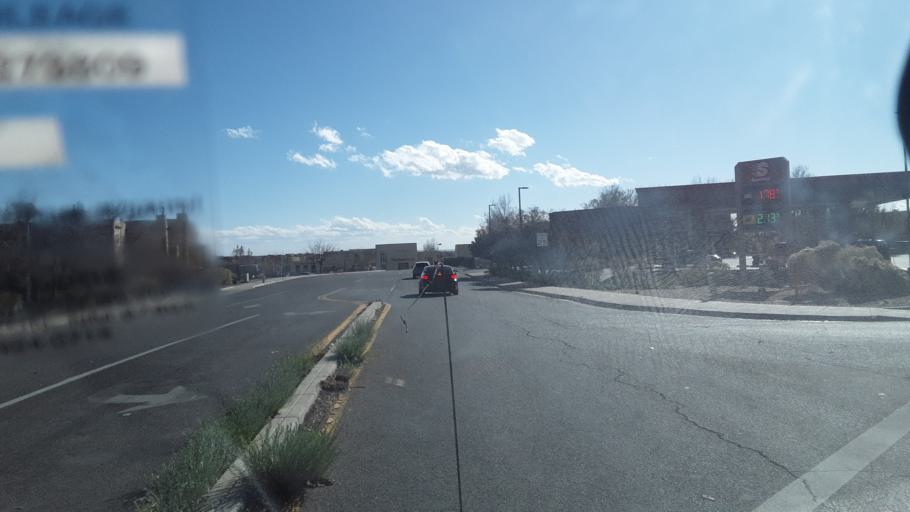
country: US
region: New Mexico
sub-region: Santa Fe County
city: Agua Fria
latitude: 35.6442
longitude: -106.0093
